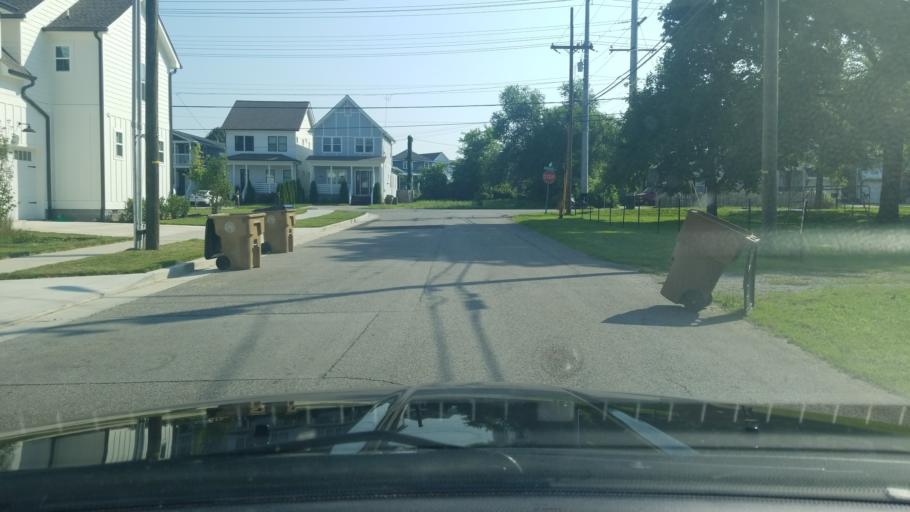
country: US
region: Tennessee
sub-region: Davidson County
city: Belle Meade
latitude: 36.1607
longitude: -86.8592
